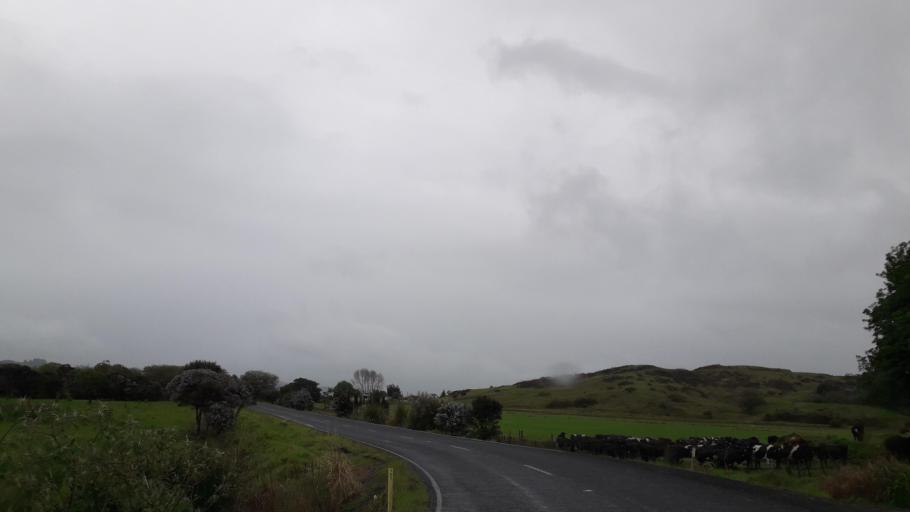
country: NZ
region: Northland
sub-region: Far North District
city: Kaitaia
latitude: -35.3680
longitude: 173.4977
